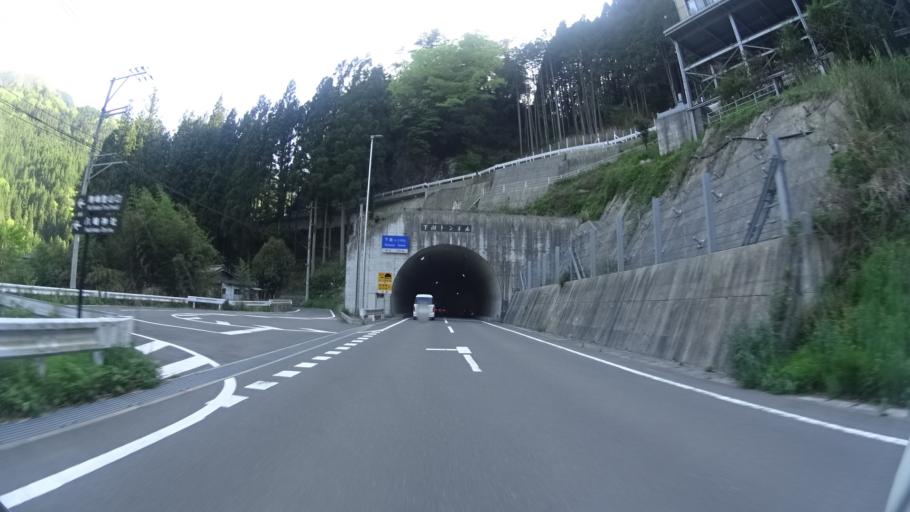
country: JP
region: Tokushima
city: Ikedacho
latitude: 33.8776
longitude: 133.9237
